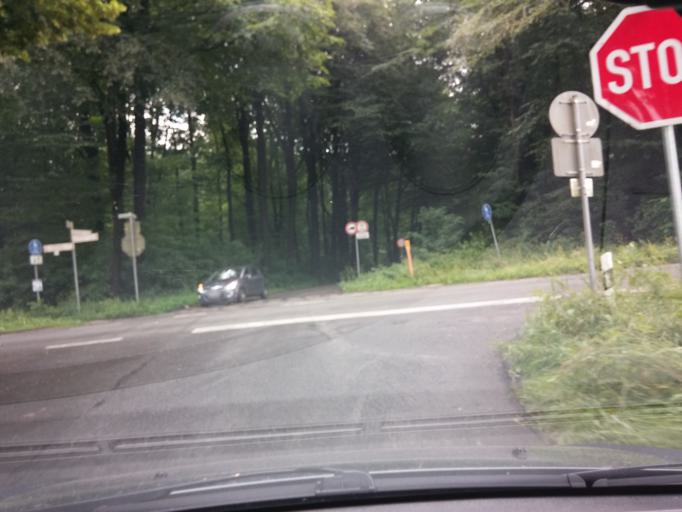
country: DE
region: North Rhine-Westphalia
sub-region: Regierungsbezirk Munster
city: Gladbeck
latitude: 51.6061
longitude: 6.9708
